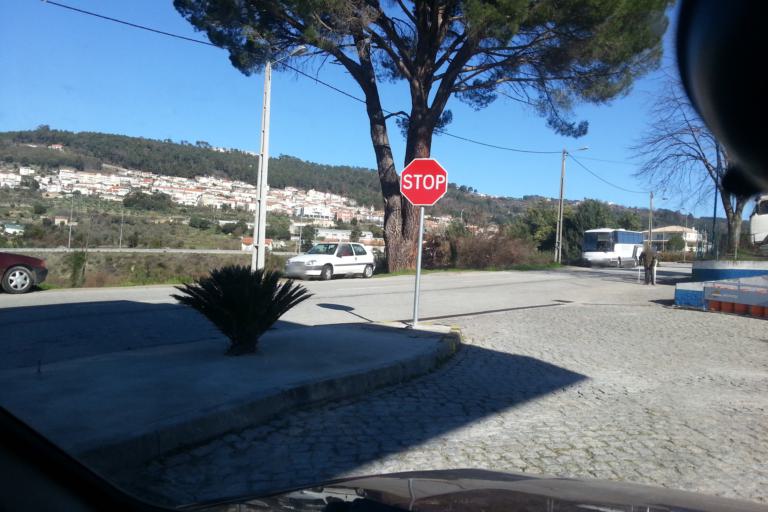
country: PT
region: Guarda
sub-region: Fornos de Algodres
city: Fornos de Algodres
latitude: 40.6129
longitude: -7.5332
